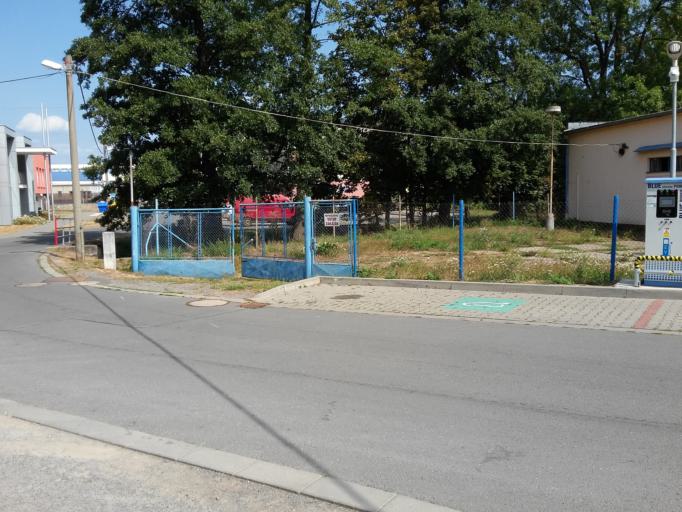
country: CZ
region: Pardubicky
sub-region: Okres Svitavy
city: Moravska Trebova
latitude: 49.7655
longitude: 16.6613
